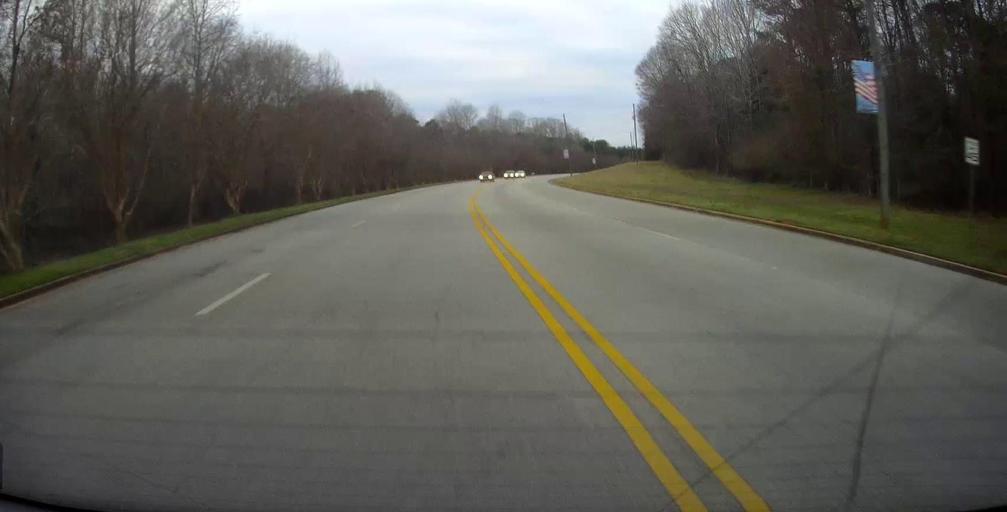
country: US
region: Alabama
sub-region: Chambers County
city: Valley
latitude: 32.8148
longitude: -85.1848
